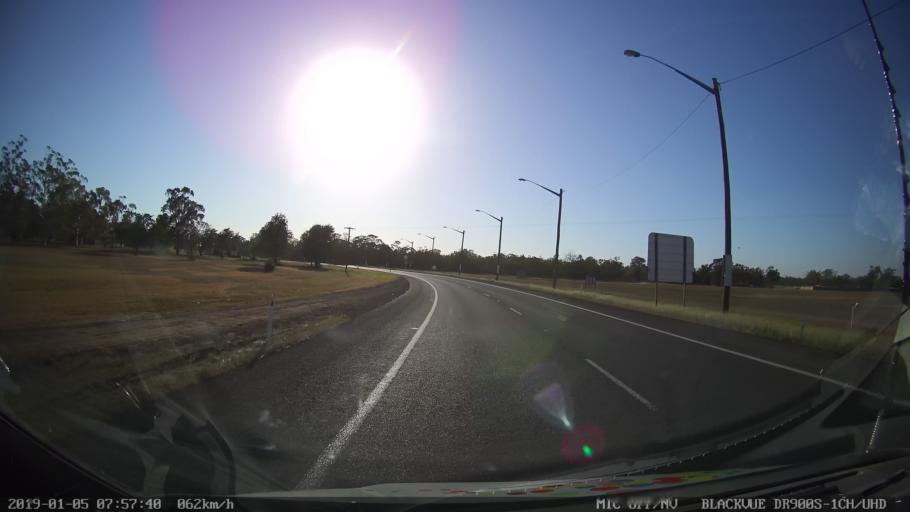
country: AU
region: New South Wales
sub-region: Gilgandra
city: Gilgandra
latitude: -31.7151
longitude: 148.6687
